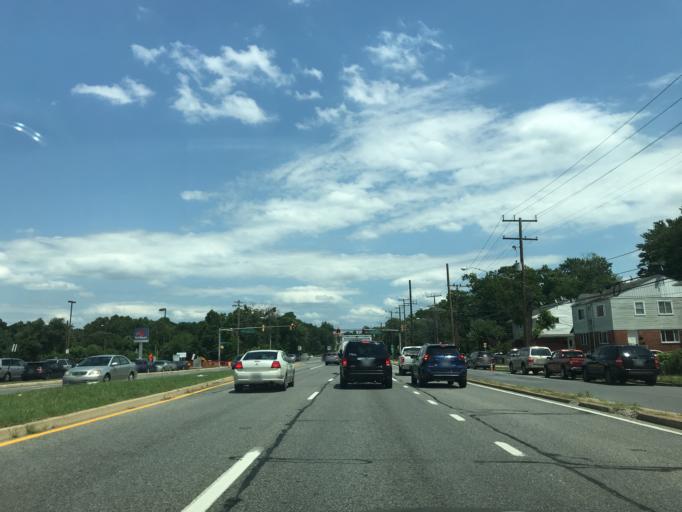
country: US
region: Maryland
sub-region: Prince George's County
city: Langley Park
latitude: 38.9845
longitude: -76.9674
